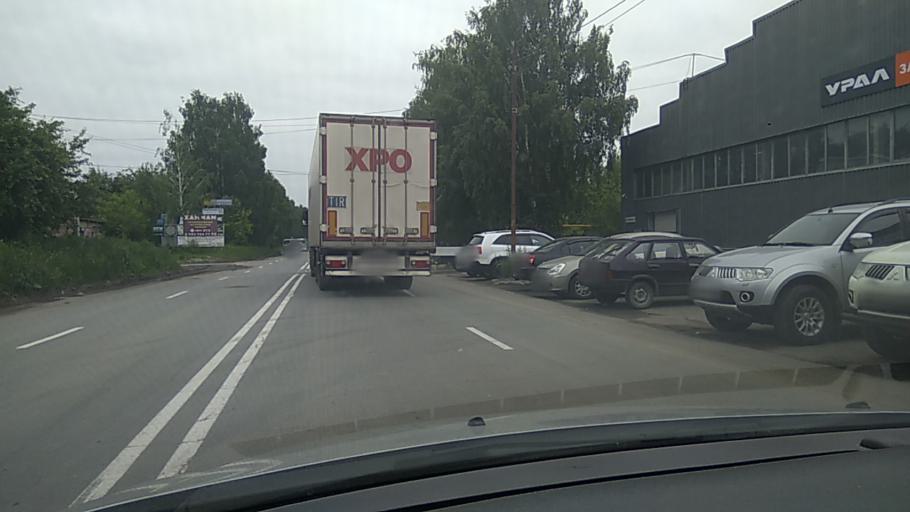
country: RU
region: Sverdlovsk
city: Shuvakish
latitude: 56.8904
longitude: 60.5203
